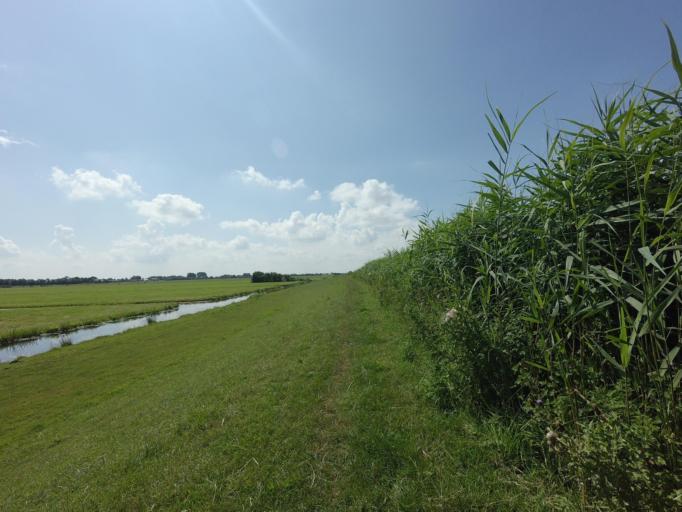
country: NL
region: South Holland
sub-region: Bodegraven-Reeuwijk
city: Bodegraven
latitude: 52.0615
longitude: 4.8047
